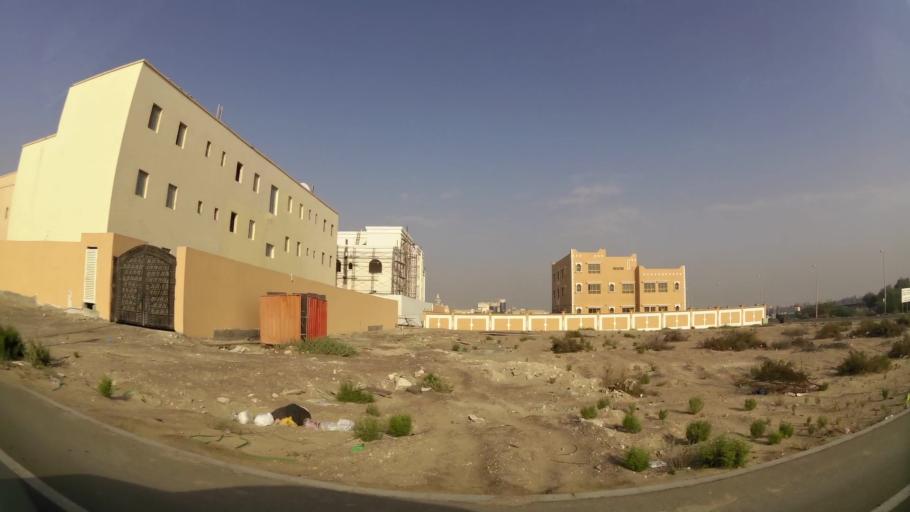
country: AE
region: Abu Dhabi
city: Abu Dhabi
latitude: 24.2732
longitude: 54.6515
